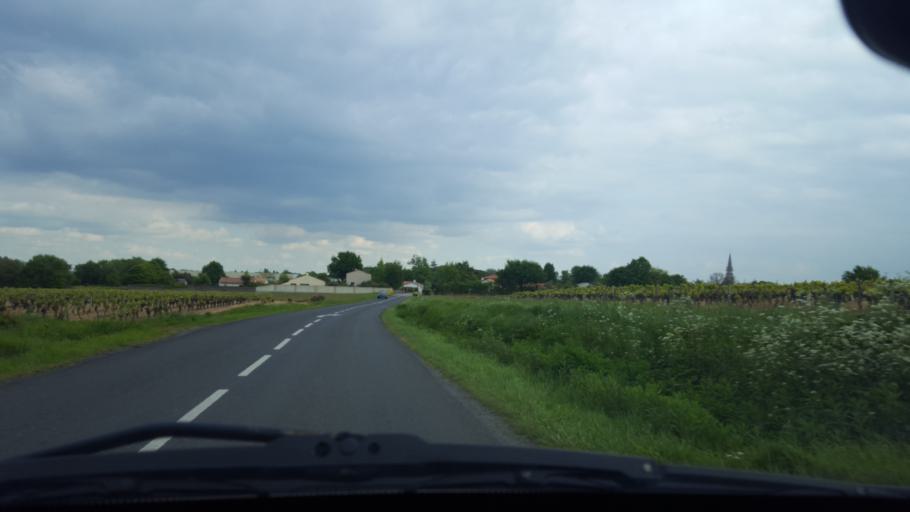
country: FR
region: Pays de la Loire
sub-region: Departement de la Loire-Atlantique
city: La Limouziniere
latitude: 46.9971
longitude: -1.6004
